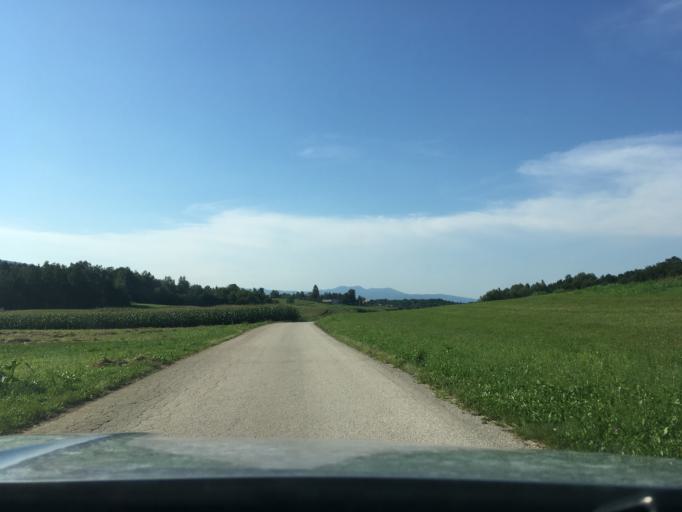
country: SI
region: Crnomelj
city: Crnomelj
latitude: 45.4647
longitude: 15.2118
